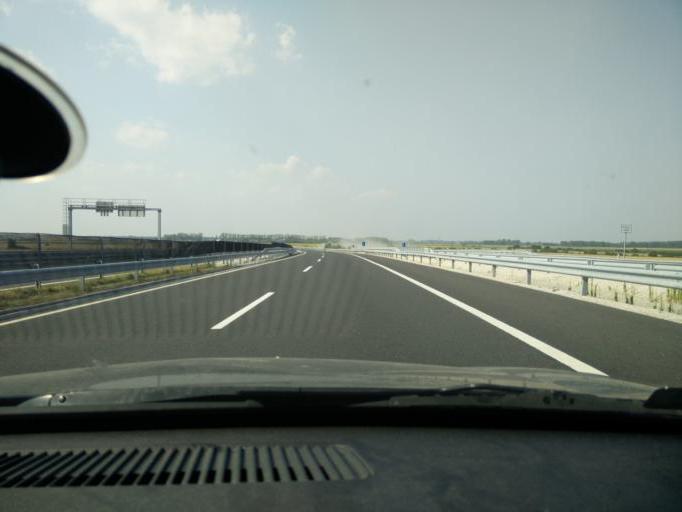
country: HU
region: Tolna
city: Tolna
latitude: 46.3842
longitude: 18.7551
